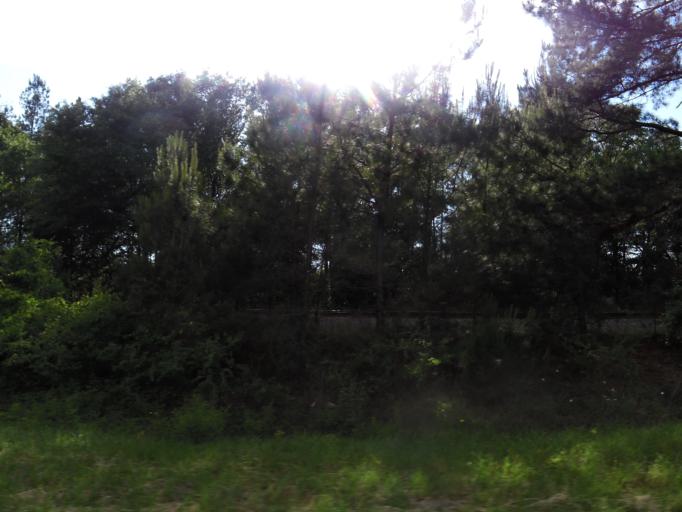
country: US
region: South Carolina
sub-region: Hampton County
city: Estill
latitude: 32.7924
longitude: -81.2405
